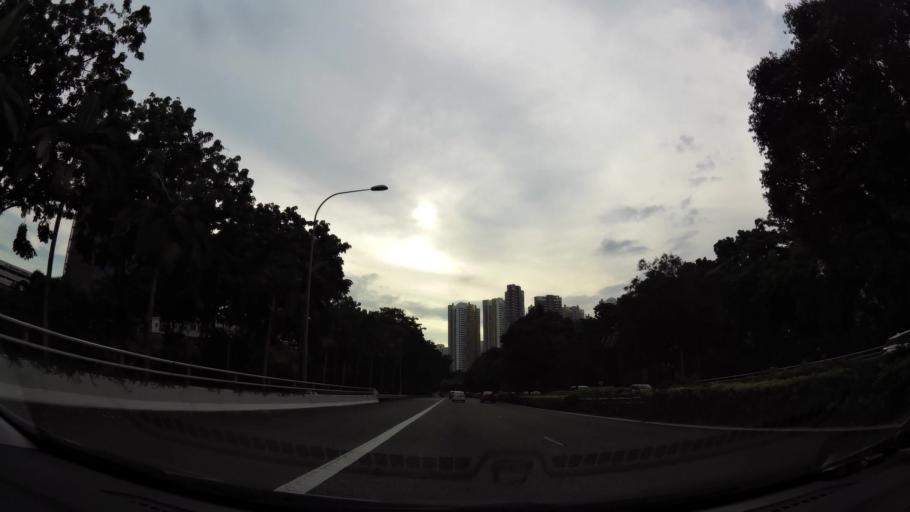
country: SG
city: Singapore
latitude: 1.2827
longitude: 103.8348
